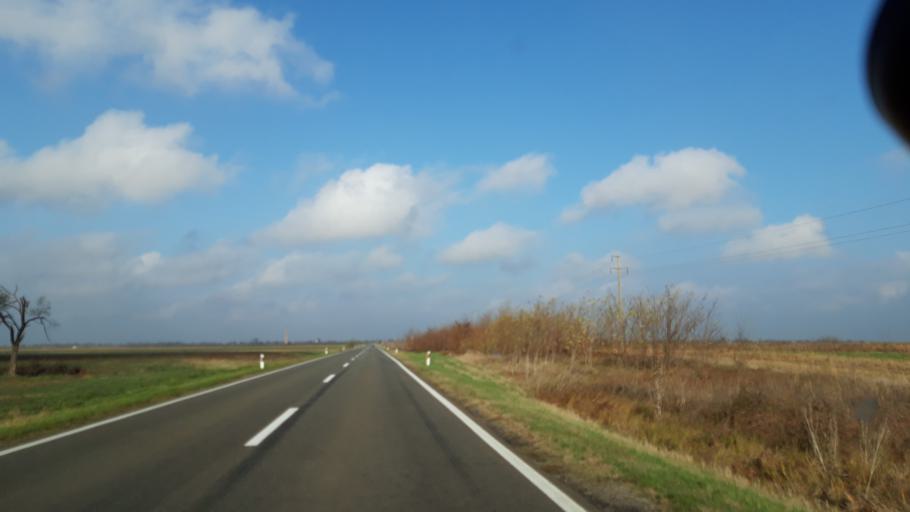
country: RS
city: Ostojicevo
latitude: 45.8704
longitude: 20.1649
